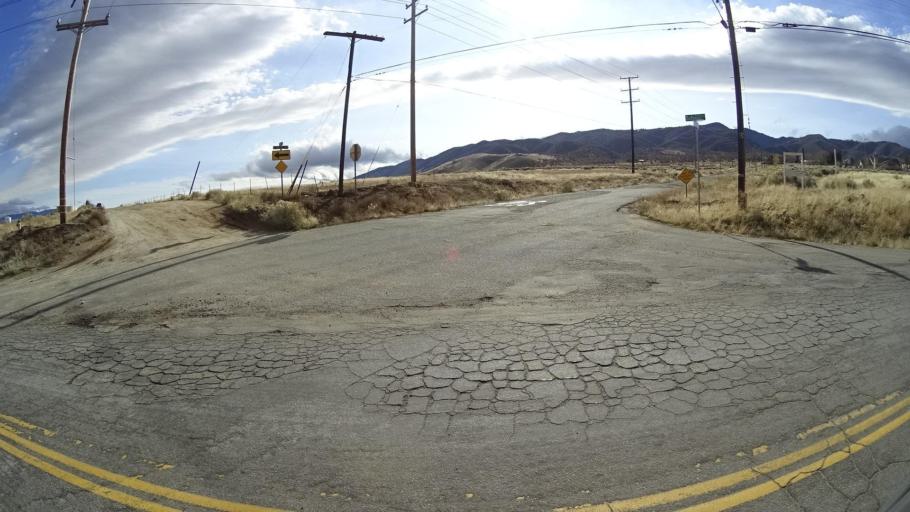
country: US
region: California
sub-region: Kern County
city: Golden Hills
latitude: 35.1175
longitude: -118.4961
